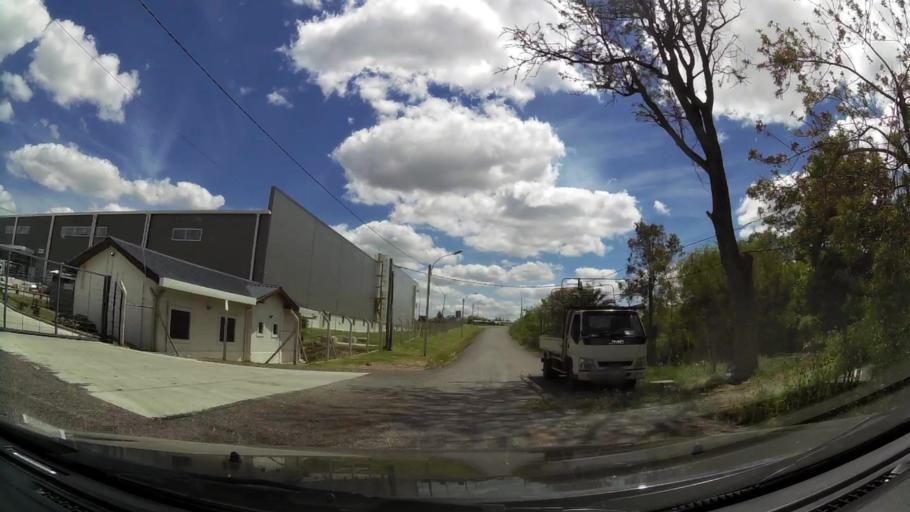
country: UY
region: Canelones
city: Colonia Nicolich
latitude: -34.8206
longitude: -56.0112
